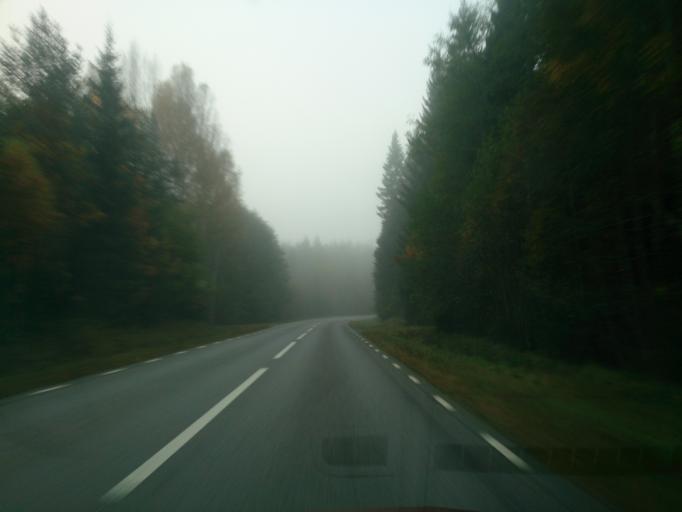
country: SE
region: OEstergoetland
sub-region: Atvidabergs Kommun
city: Atvidaberg
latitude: 58.0872
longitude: 15.9452
